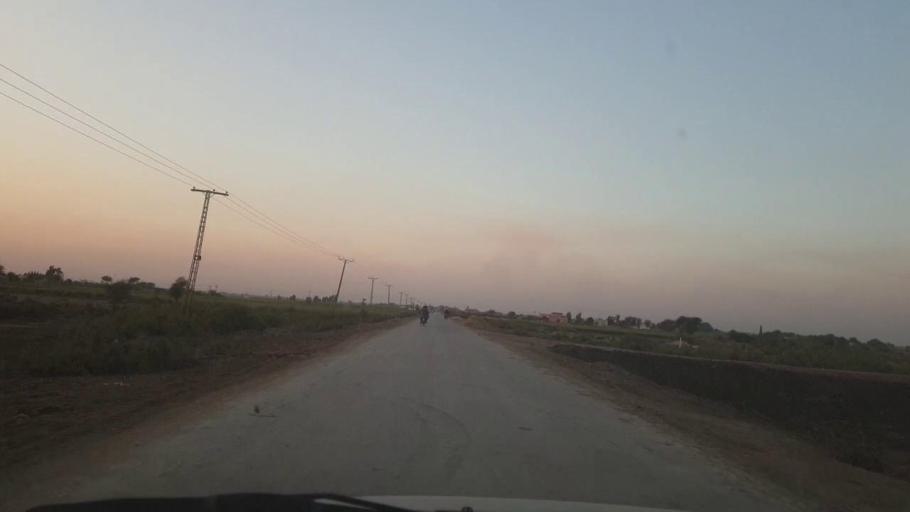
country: PK
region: Sindh
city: Mirpur Khas
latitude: 25.4903
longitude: 69.0404
